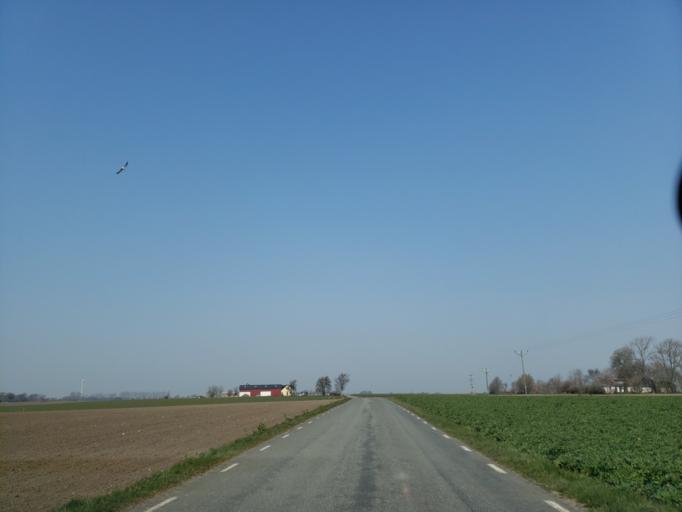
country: SE
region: Skane
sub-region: Simrishamns Kommun
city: Simrishamn
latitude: 55.4549
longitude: 14.2143
